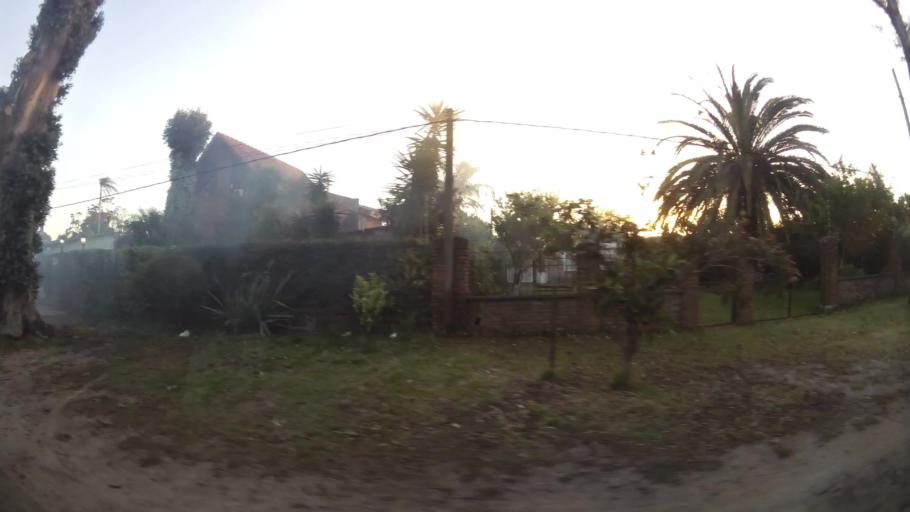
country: UY
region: Canelones
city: Barra de Carrasco
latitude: -34.8470
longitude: -55.9806
